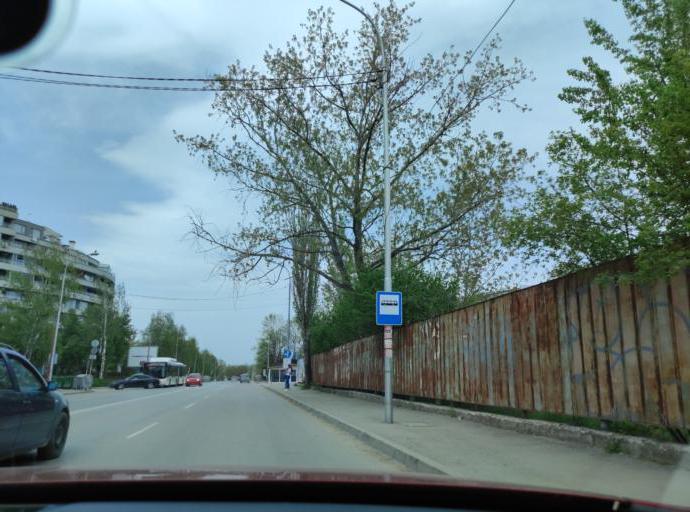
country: BG
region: Sofia-Capital
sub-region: Stolichna Obshtina
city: Sofia
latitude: 42.6488
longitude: 23.3462
